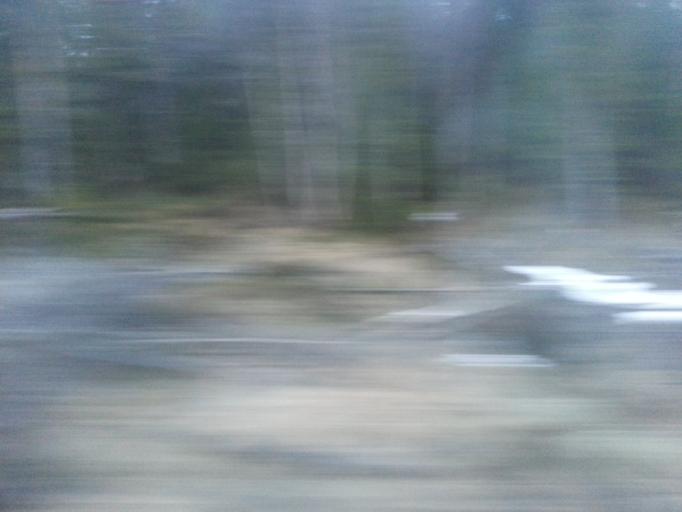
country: NO
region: Sor-Trondelag
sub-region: Rennebu
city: Berkak
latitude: 62.7829
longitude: 9.9942
